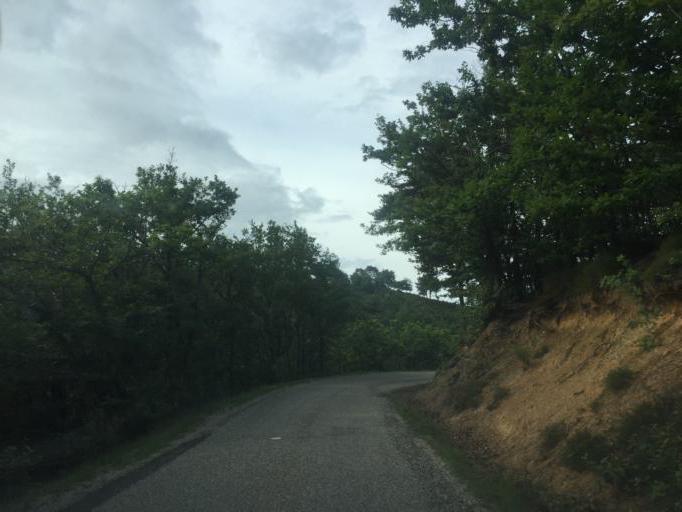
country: FR
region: Rhone-Alpes
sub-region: Departement de l'Ardeche
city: Flaviac
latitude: 44.7933
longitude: 4.6574
